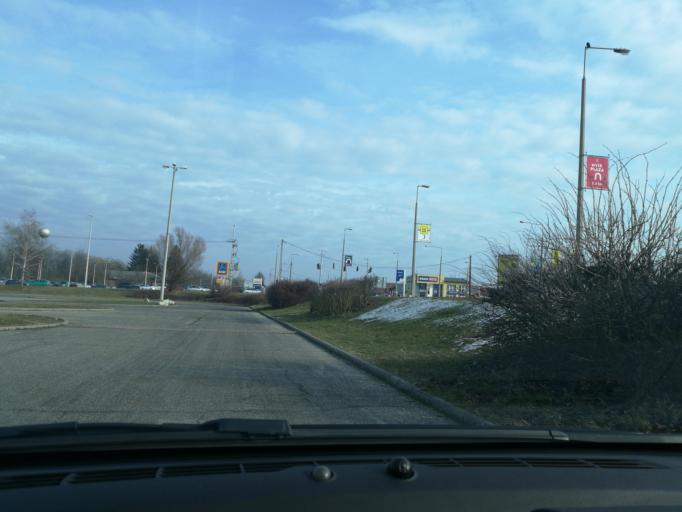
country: HU
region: Szabolcs-Szatmar-Bereg
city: Nyiregyhaza
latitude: 47.9700
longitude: 21.7393
